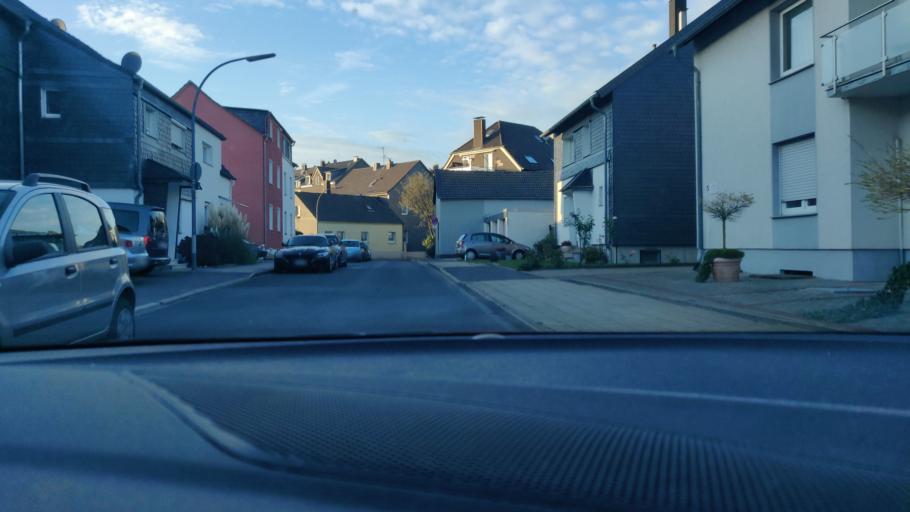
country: DE
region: North Rhine-Westphalia
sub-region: Regierungsbezirk Dusseldorf
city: Velbert
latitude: 51.3281
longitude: 7.0618
